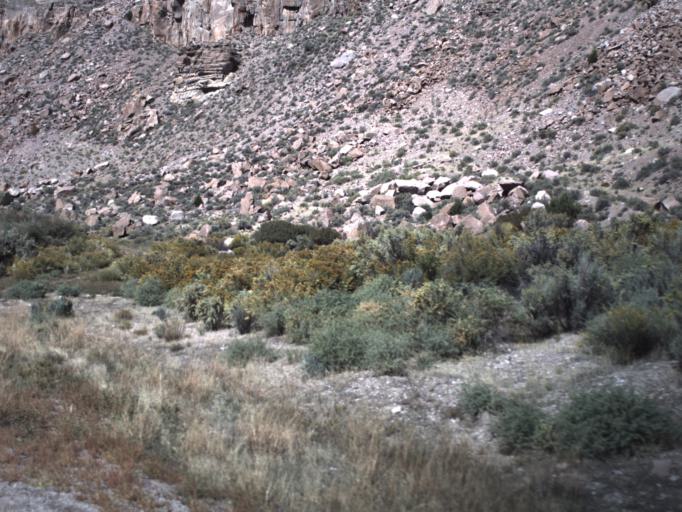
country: US
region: Utah
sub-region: Piute County
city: Junction
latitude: 38.1972
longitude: -112.1227
